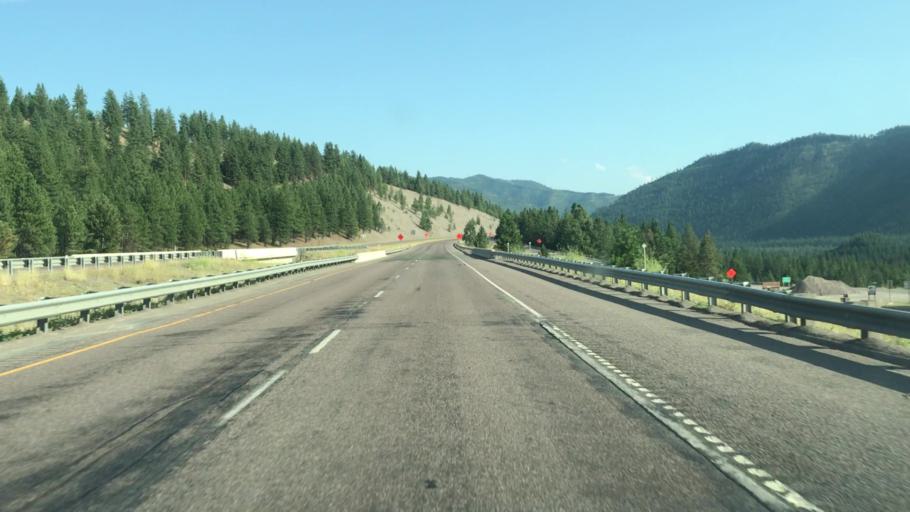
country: US
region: Montana
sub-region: Mineral County
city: Superior
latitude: 47.0266
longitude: -114.7399
